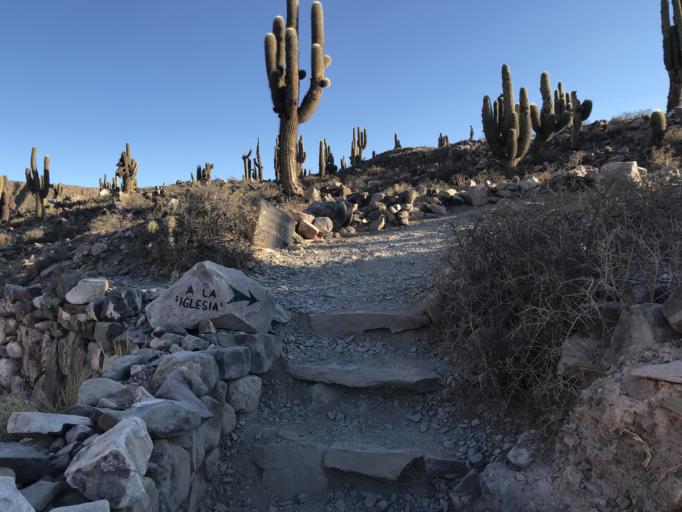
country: AR
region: Jujuy
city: Maimara
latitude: -23.5855
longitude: -65.4006
